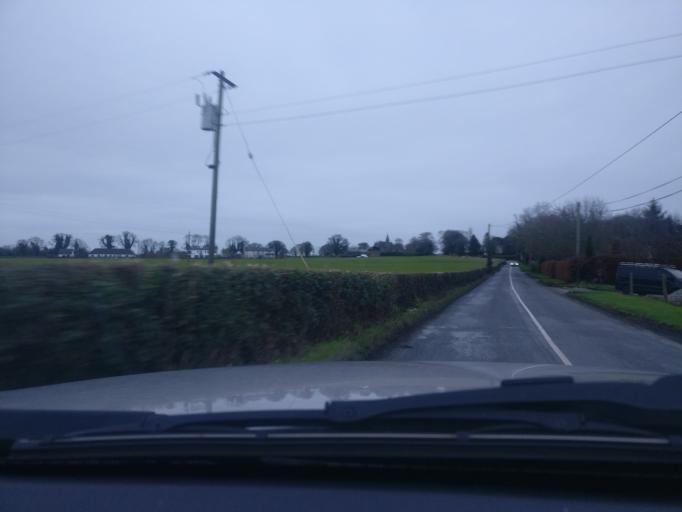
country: IE
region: Leinster
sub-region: An Mhi
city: Dunshaughlin
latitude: 53.4940
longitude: -6.6027
